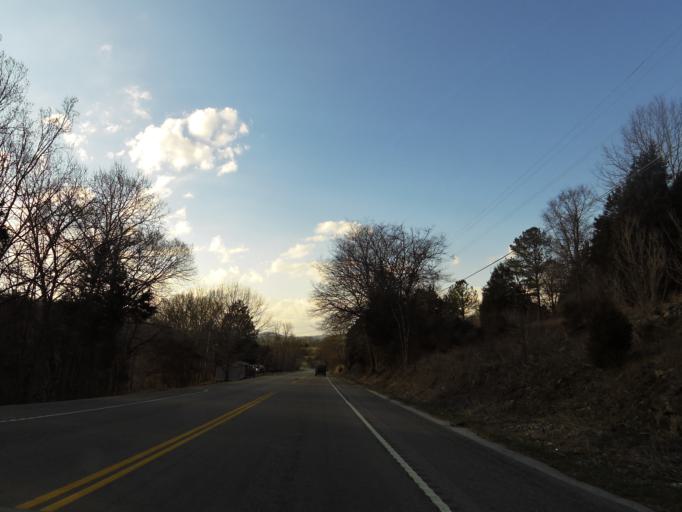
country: US
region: Tennessee
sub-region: Smith County
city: South Carthage
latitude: 36.2483
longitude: -86.0340
